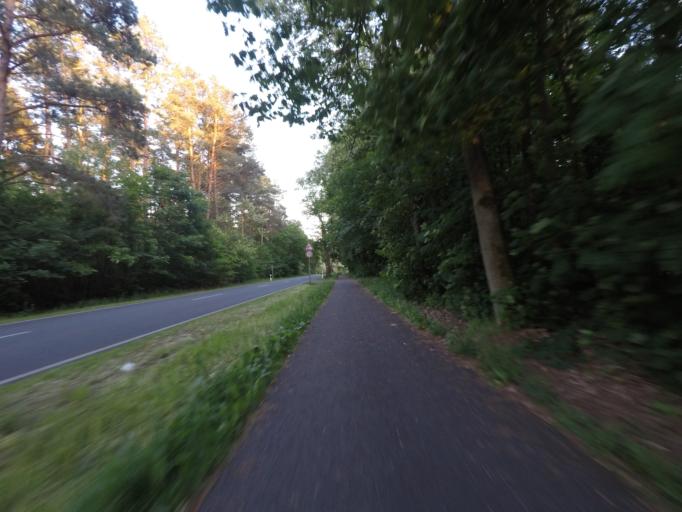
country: DE
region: Brandenburg
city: Marienwerder
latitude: 52.8603
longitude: 13.6488
